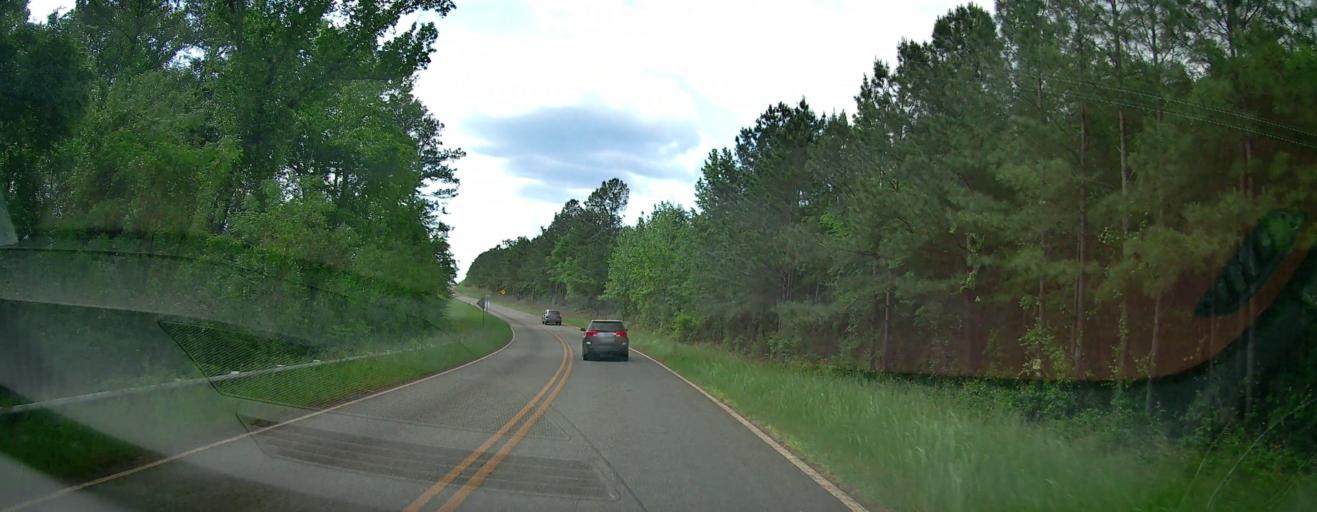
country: US
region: Georgia
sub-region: Laurens County
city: East Dublin
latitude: 32.7335
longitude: -82.9099
